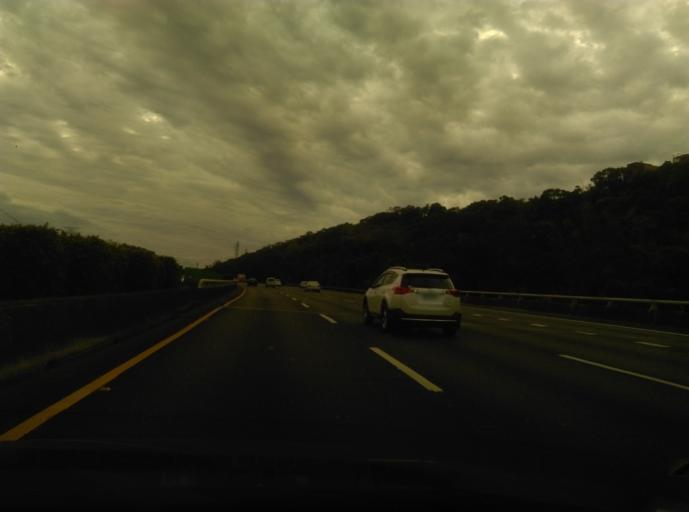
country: TW
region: Taiwan
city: Daxi
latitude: 24.9201
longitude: 121.2977
